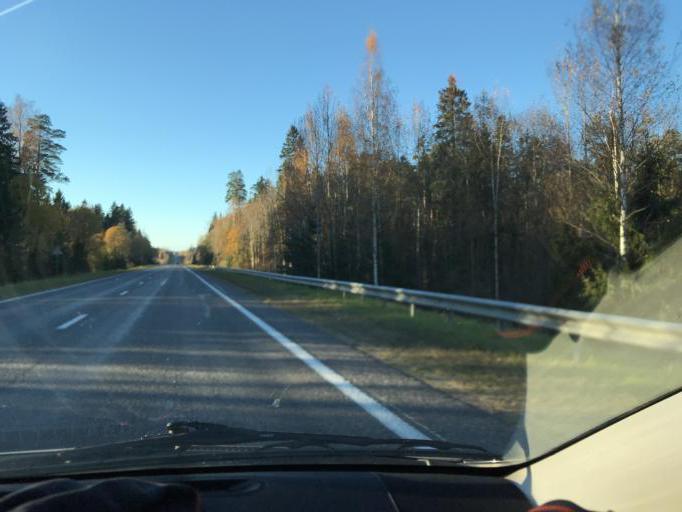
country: BY
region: Vitebsk
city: Vitebsk
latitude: 55.3411
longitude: 30.2329
